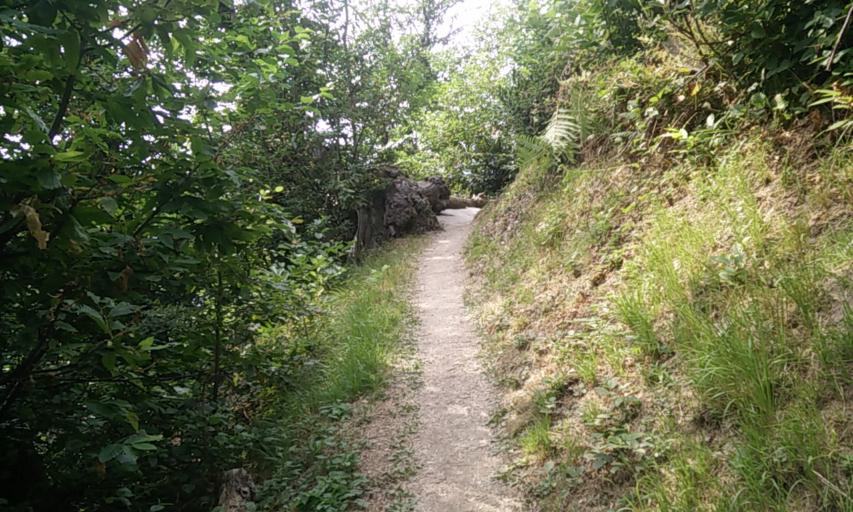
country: IT
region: Tuscany
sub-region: Provincia di Lucca
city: Pontestazzemese
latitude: 43.9942
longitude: 10.3330
